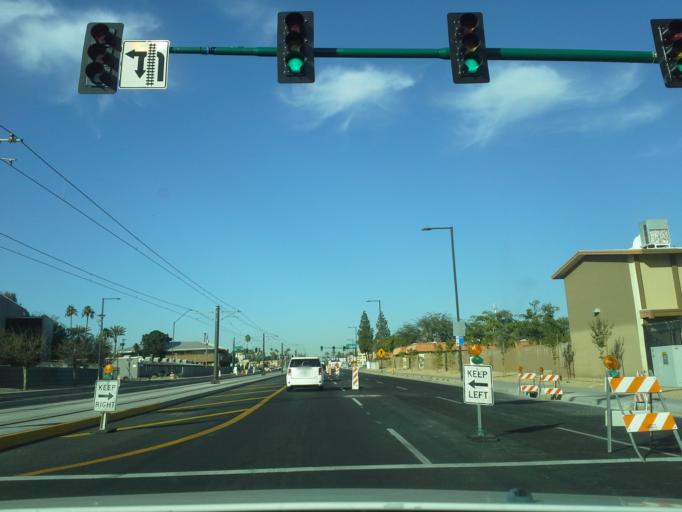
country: US
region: Arizona
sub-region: Maricopa County
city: Glendale
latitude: 33.5496
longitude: -112.0995
